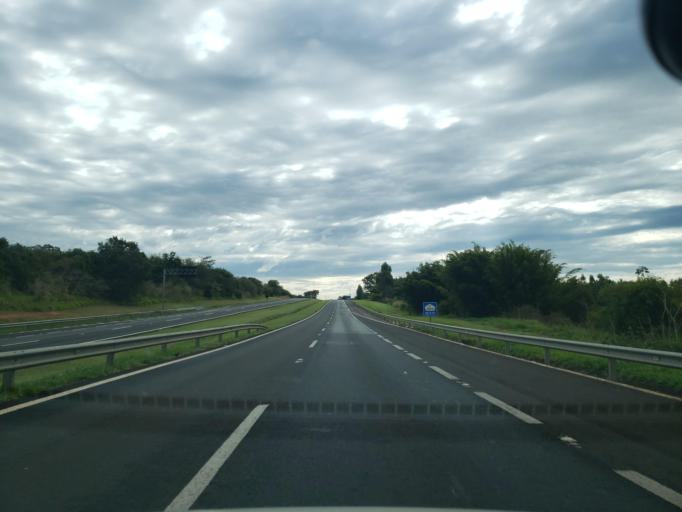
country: BR
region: Sao Paulo
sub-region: Bauru
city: Bauru
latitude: -22.2038
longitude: -49.1843
